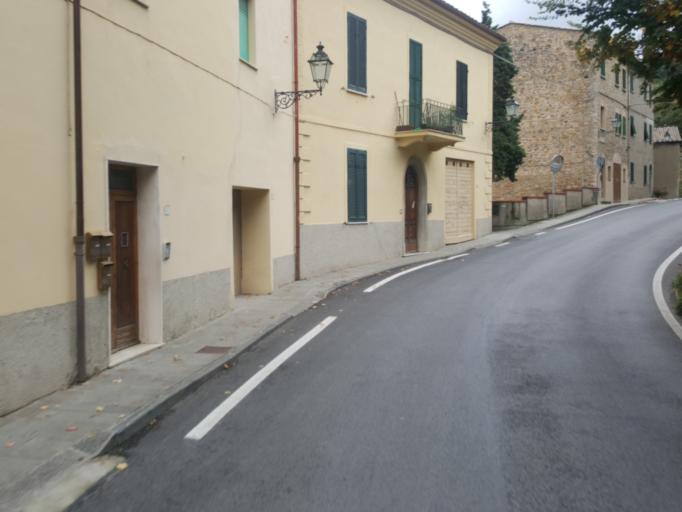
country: IT
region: Tuscany
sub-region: Province of Pisa
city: Castelnuovo di Val di Cecina
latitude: 43.2073
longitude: 10.9060
